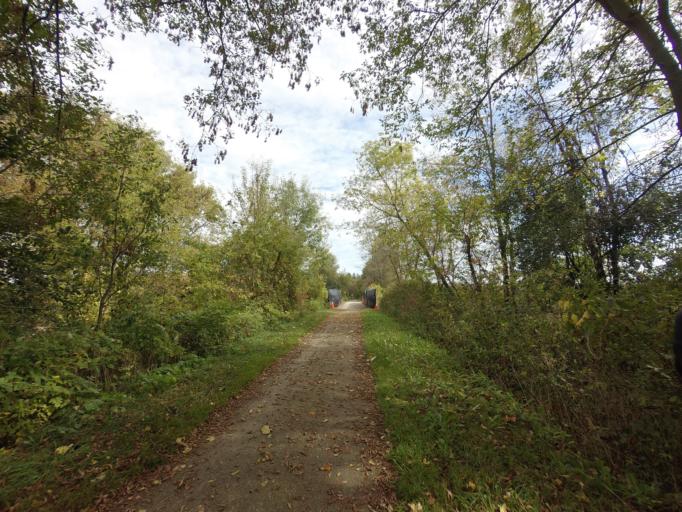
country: CA
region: Ontario
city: Ancaster
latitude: 43.2207
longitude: -80.0602
